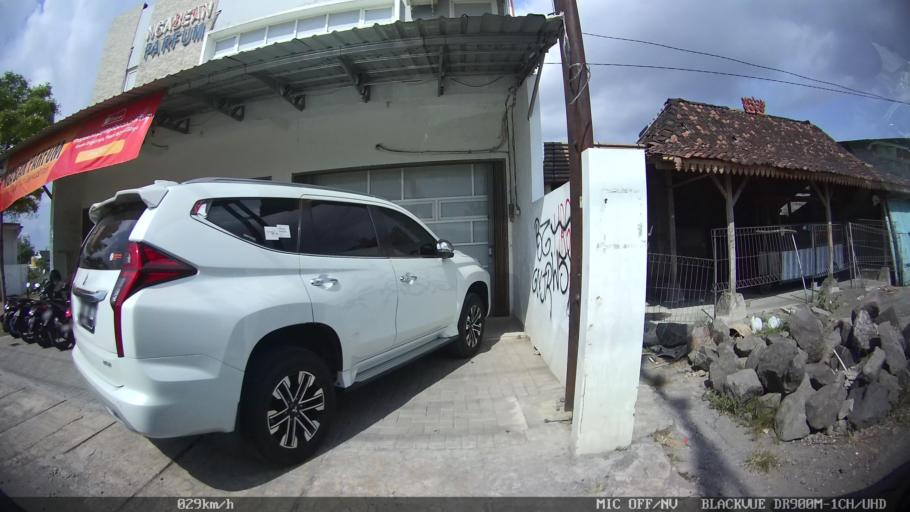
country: ID
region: Daerah Istimewa Yogyakarta
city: Kasihan
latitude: -7.8166
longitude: 110.3284
